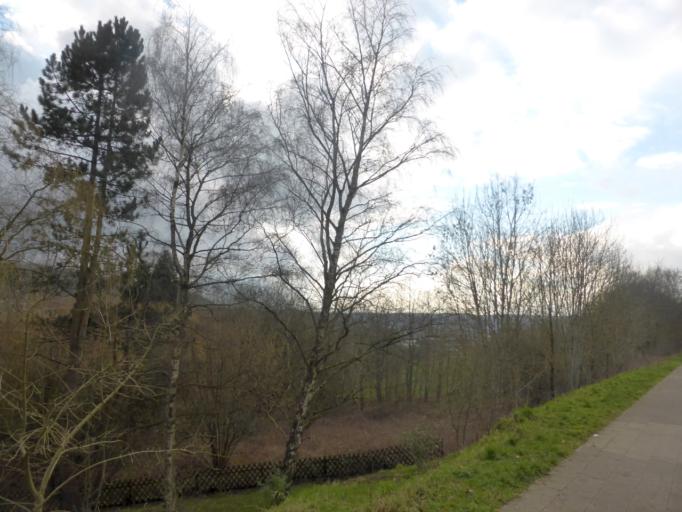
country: LU
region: Luxembourg
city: Belvaux
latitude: 49.5181
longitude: 5.9333
